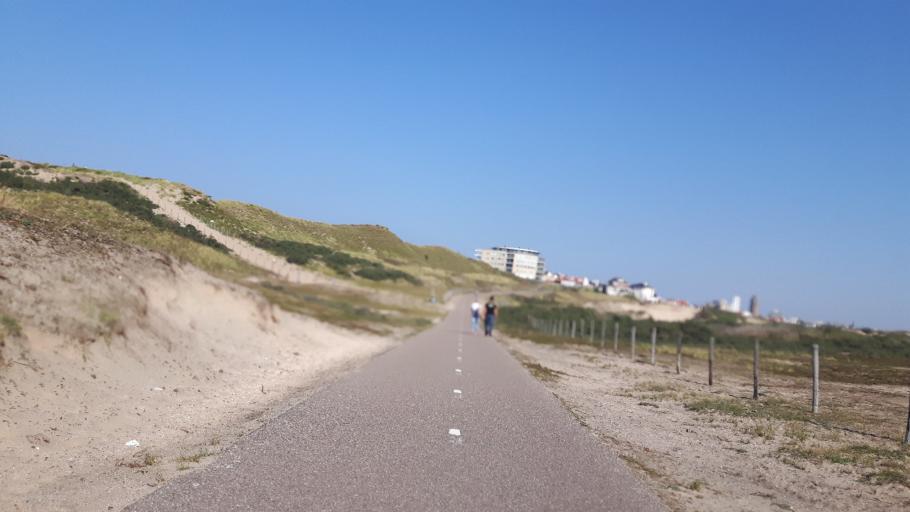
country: NL
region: North Holland
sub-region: Gemeente Zandvoort
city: Zandvoort
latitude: 52.3578
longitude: 4.5179
